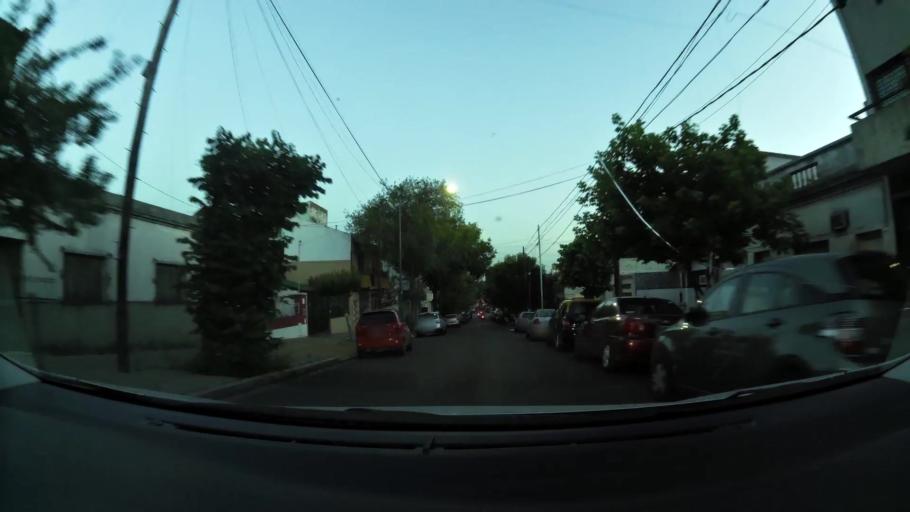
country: AR
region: Buenos Aires F.D.
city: Villa Lugano
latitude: -34.6837
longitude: -58.4770
